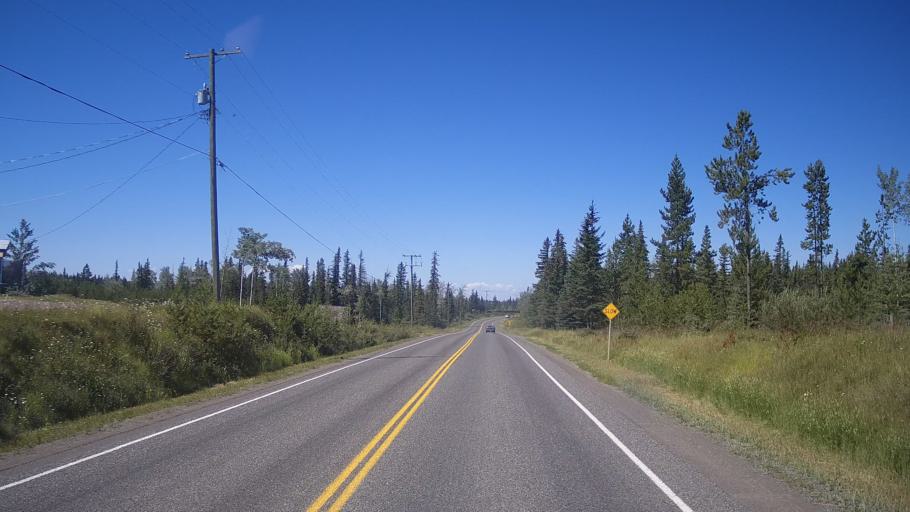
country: CA
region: British Columbia
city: Cache Creek
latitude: 51.5525
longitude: -121.2255
